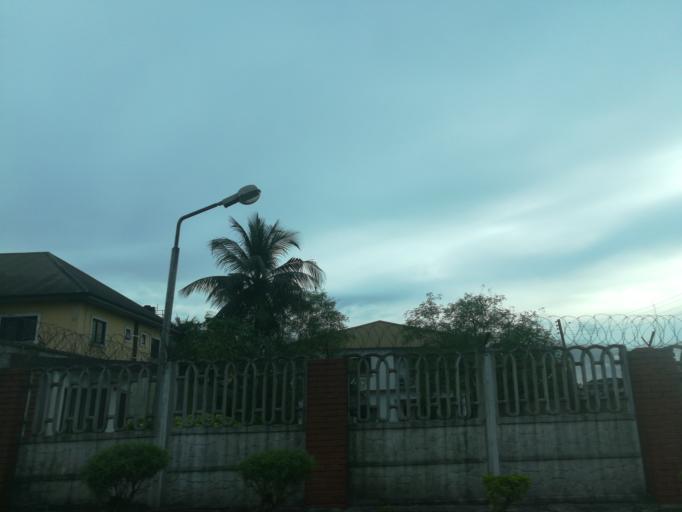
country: NG
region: Rivers
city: Port Harcourt
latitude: 4.8135
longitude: 7.0001
